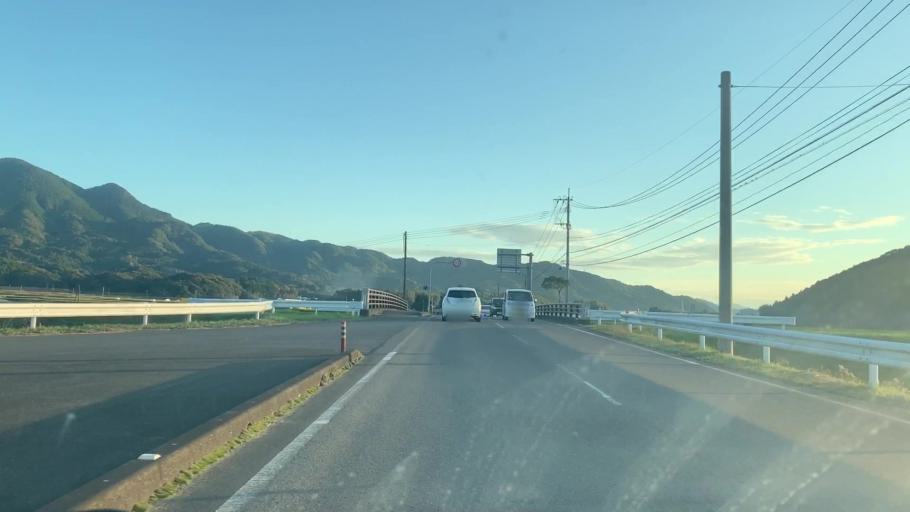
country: JP
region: Saga Prefecture
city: Imaricho-ko
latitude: 33.2998
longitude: 129.9698
